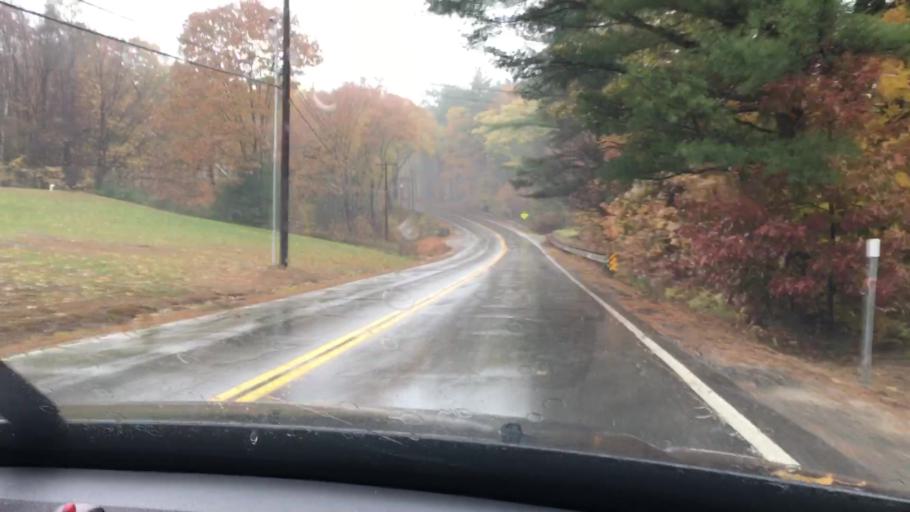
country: US
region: New Hampshire
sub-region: Belknap County
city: Meredith
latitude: 43.7121
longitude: -71.5260
